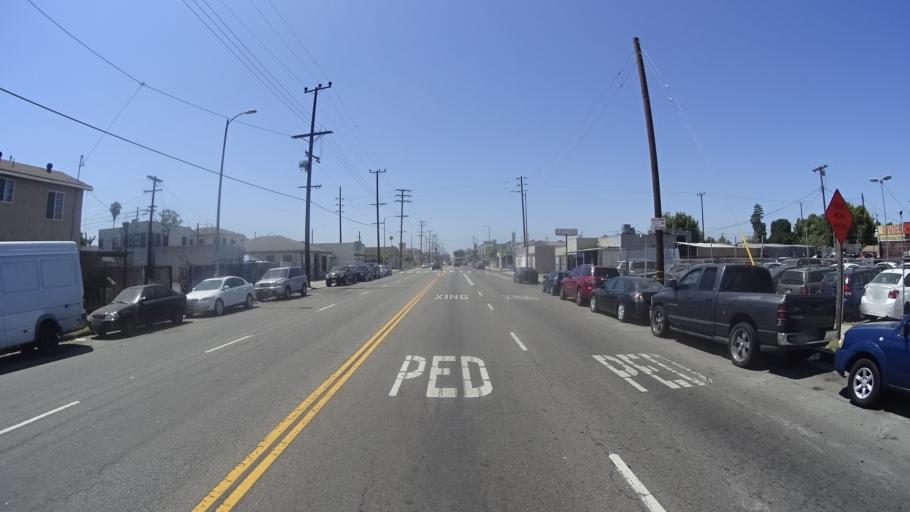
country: US
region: California
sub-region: Los Angeles County
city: Westmont
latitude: 33.9841
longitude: -118.3003
